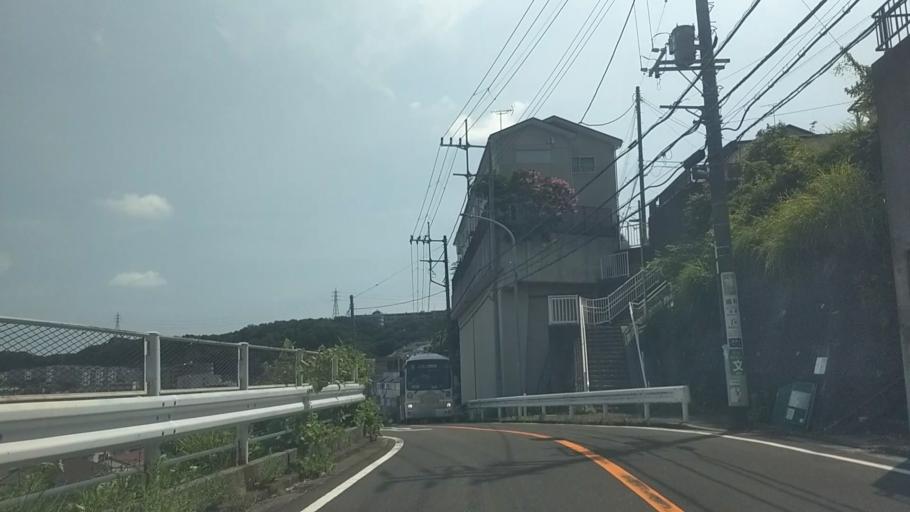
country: JP
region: Kanagawa
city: Zushi
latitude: 35.3348
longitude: 139.6045
